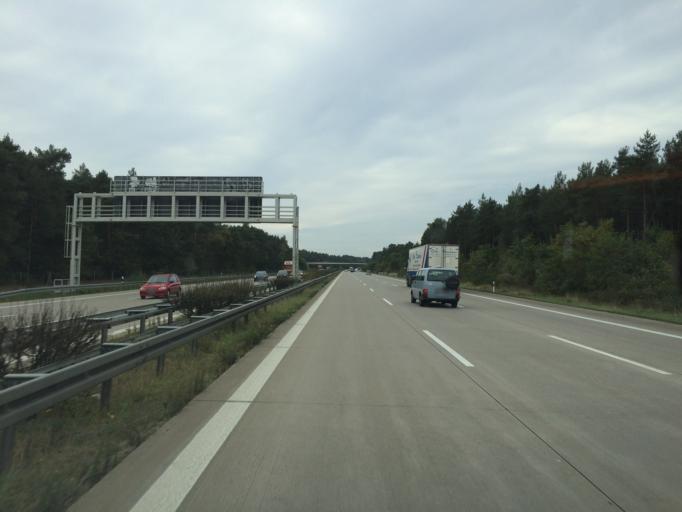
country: DE
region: Brandenburg
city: Wollin
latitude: 52.2857
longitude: 12.4524
